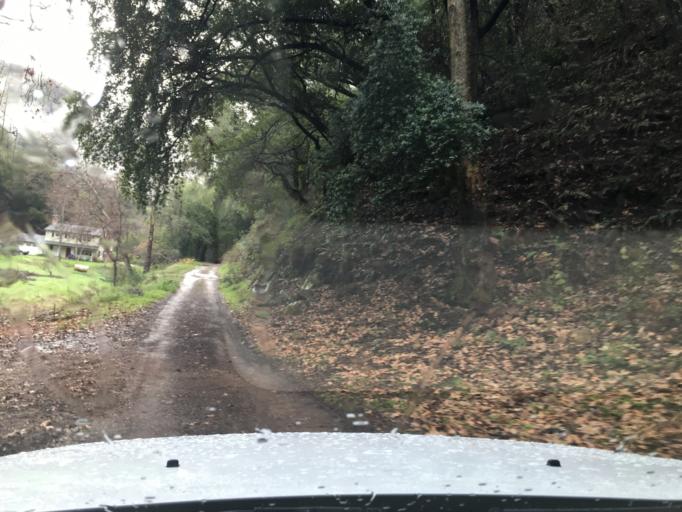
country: US
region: California
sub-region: San Luis Obispo County
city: Avila Beach
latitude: 35.2258
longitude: -120.7556
